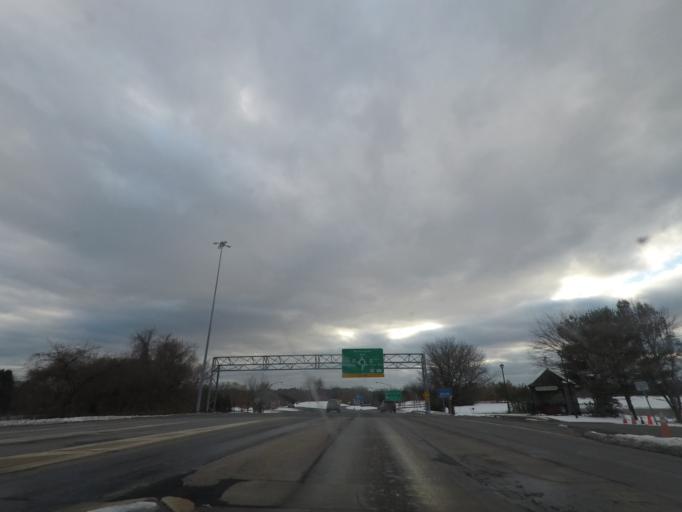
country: US
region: New York
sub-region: Ulster County
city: Lincoln Park
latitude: 41.9452
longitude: -74.0268
